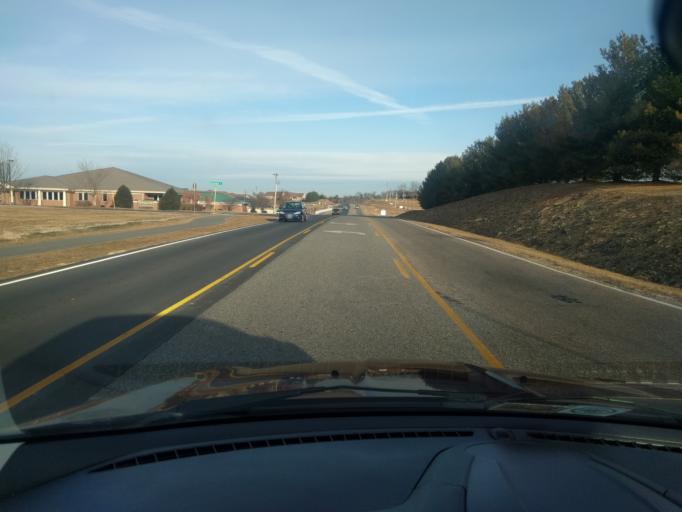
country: US
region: Virginia
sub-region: Augusta County
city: Fishersville
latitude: 38.0923
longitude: -78.9888
